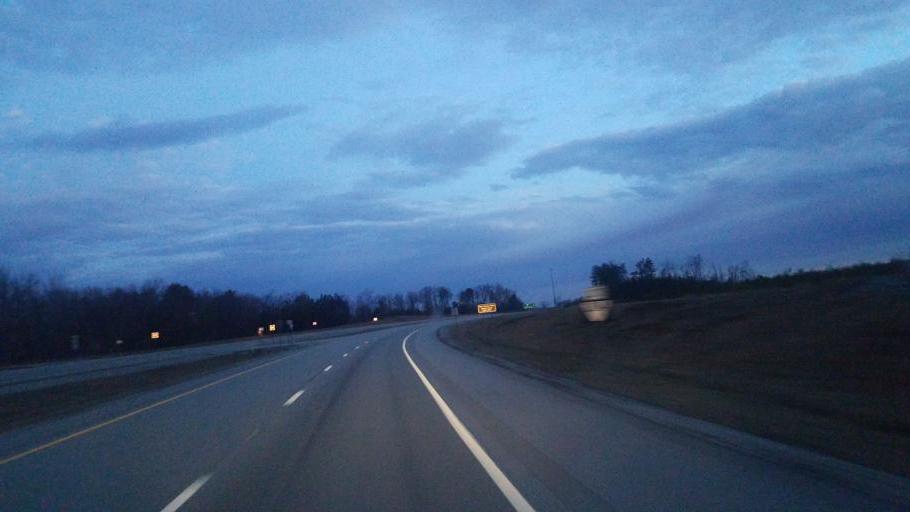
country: US
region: Tennessee
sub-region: Van Buren County
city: Spencer
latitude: 35.6214
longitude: -85.4760
